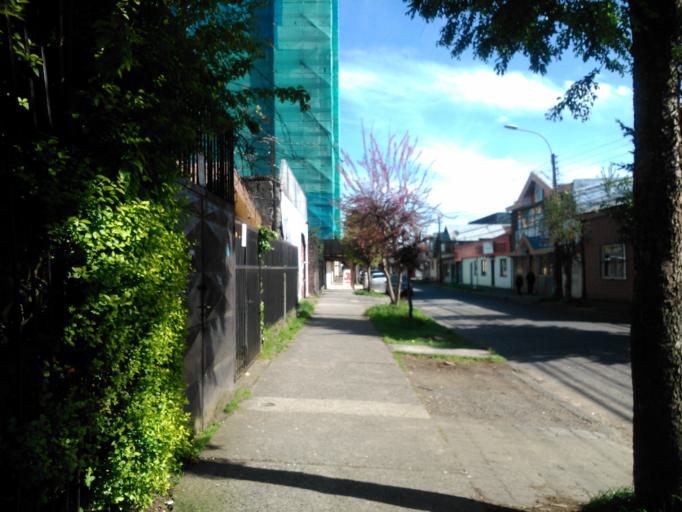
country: CL
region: Araucania
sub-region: Provincia de Cautin
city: Temuco
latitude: -38.7398
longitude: -72.5961
